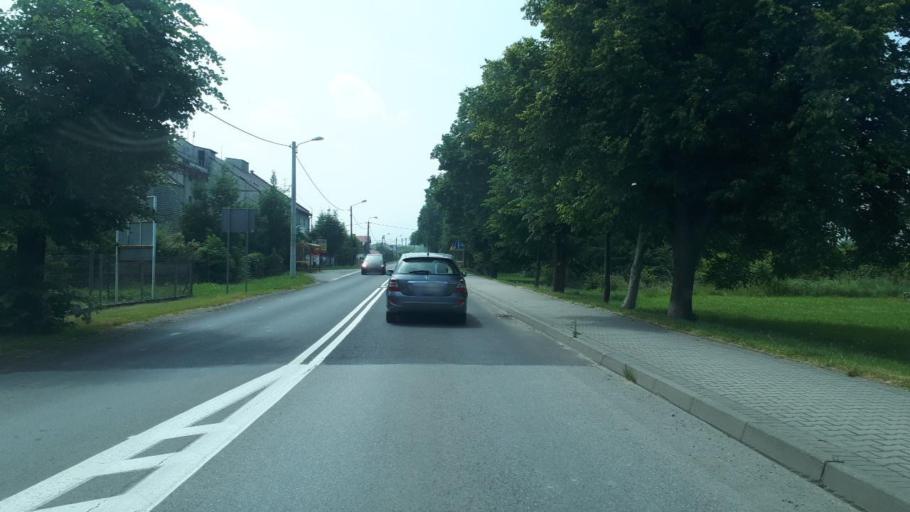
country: PL
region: Silesian Voivodeship
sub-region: Powiat cieszynski
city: Ustron
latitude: 49.7453
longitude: 18.8036
